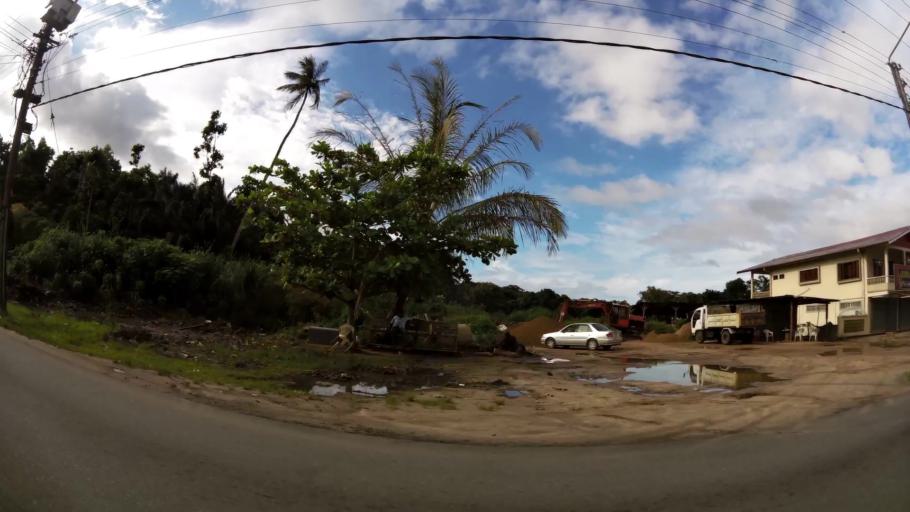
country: SR
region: Paramaribo
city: Paramaribo
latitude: 5.8451
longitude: -55.2232
